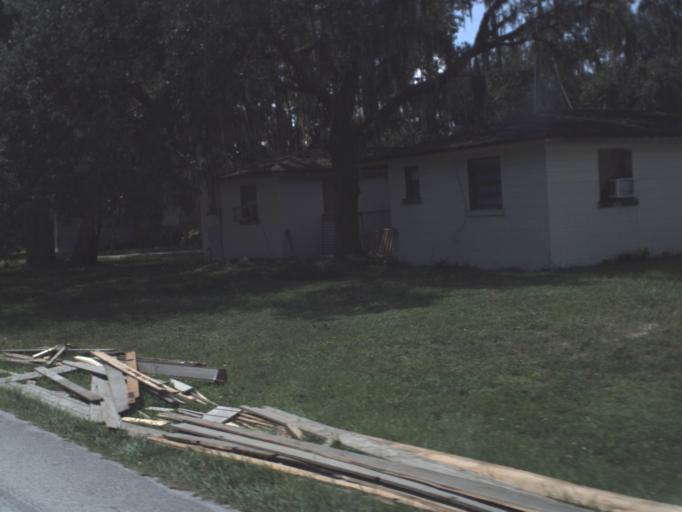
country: US
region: Florida
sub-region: Highlands County
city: Avon Park
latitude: 27.5634
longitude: -81.4537
